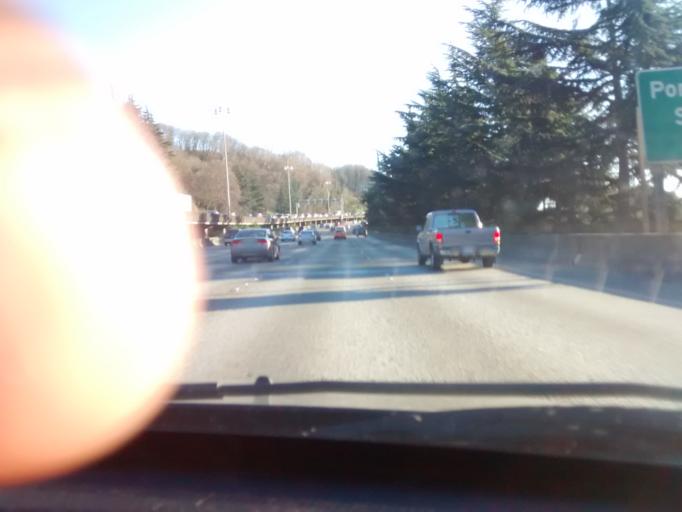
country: US
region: Washington
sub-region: King County
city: Seattle
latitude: 47.5822
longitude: -122.3199
